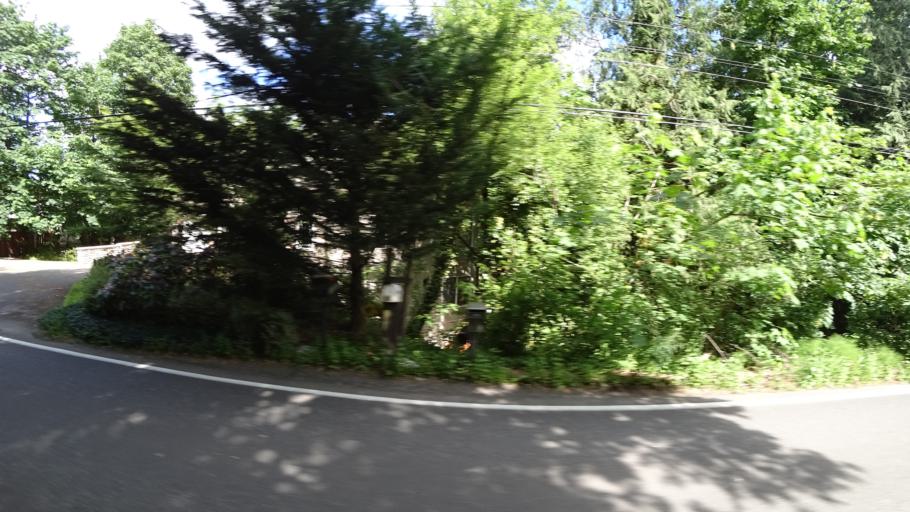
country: US
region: Oregon
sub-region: Washington County
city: Bethany
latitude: 45.6028
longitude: -122.8327
